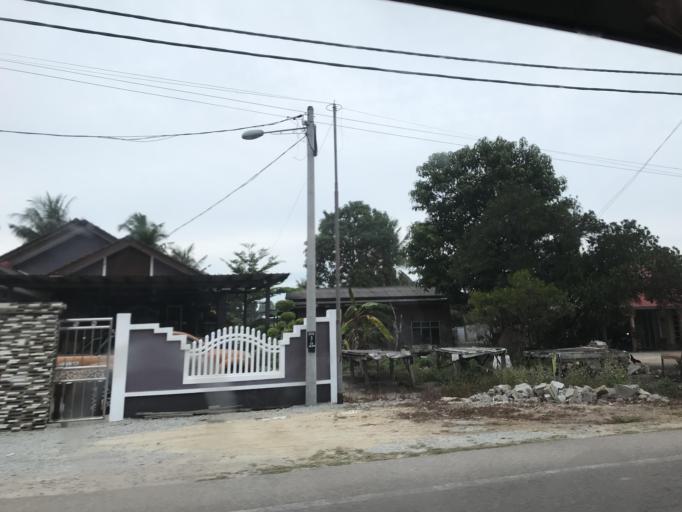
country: MY
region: Kelantan
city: Kota Bharu
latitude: 6.1748
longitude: 102.2148
